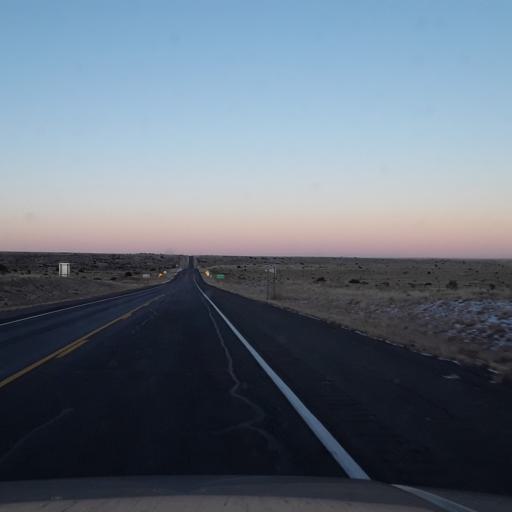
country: US
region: New Mexico
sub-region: Guadalupe County
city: Santa Rosa
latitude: 34.5357
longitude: -105.3147
